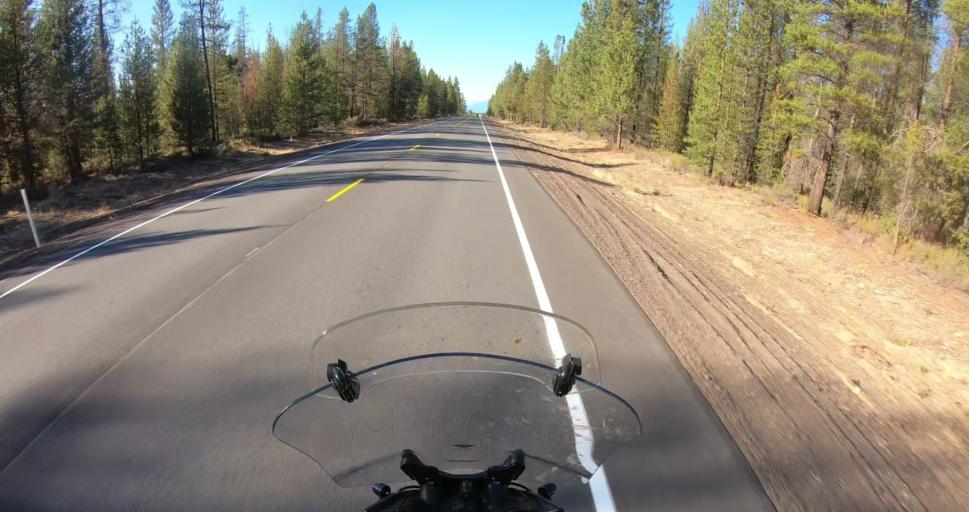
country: US
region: Oregon
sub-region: Deschutes County
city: La Pine
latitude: 43.5563
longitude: -121.4745
